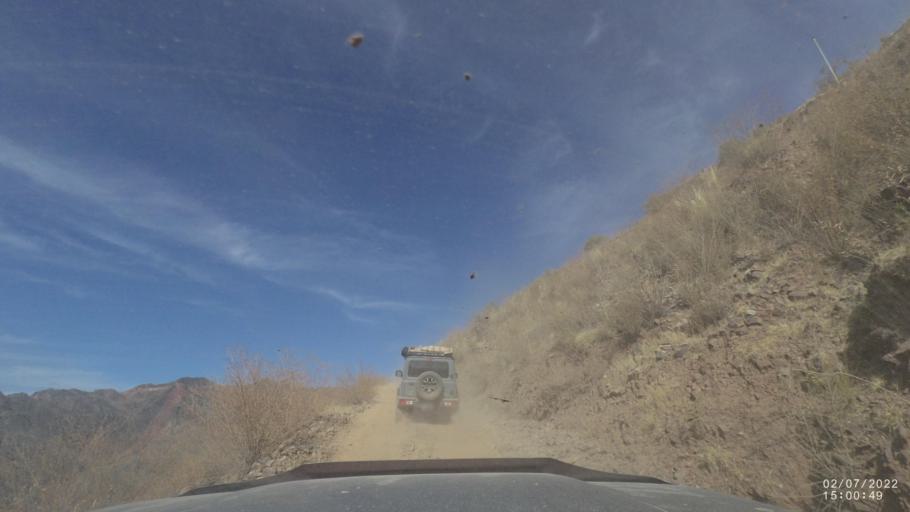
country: BO
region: Cochabamba
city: Irpa Irpa
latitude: -17.8523
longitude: -66.4425
